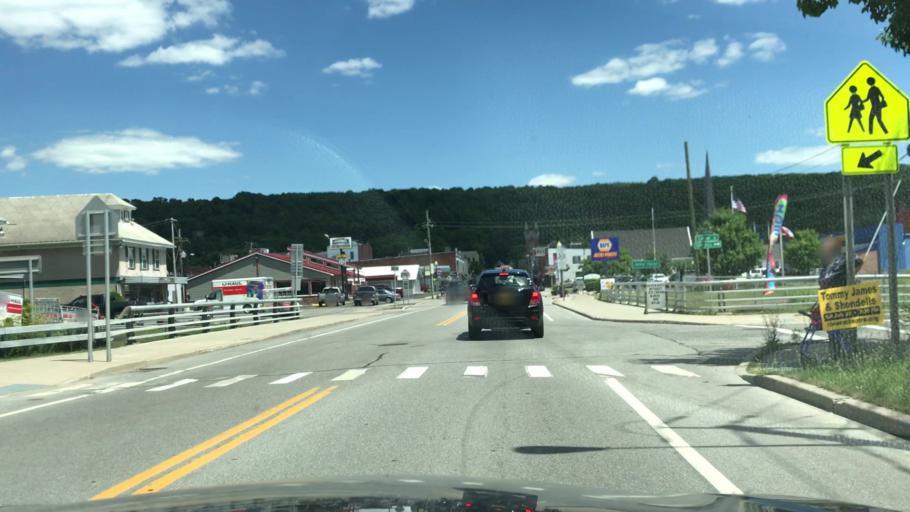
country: US
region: New York
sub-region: Wyoming County
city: Warsaw
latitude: 42.7403
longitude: -78.1363
